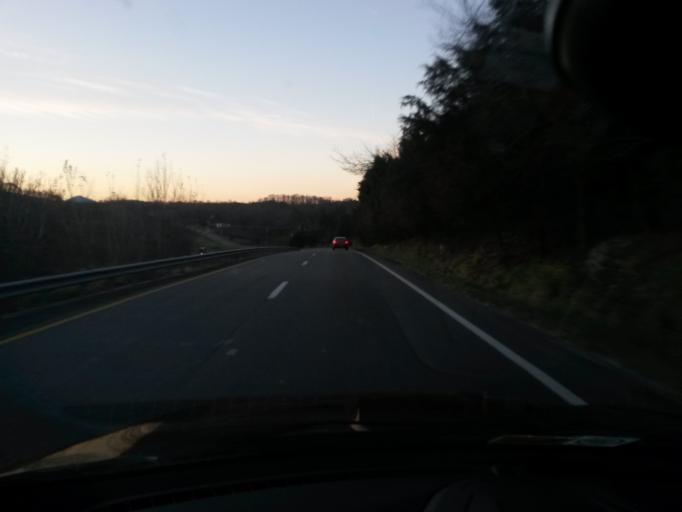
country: US
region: Virginia
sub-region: Botetourt County
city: Fincastle
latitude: 37.4726
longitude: -79.8818
